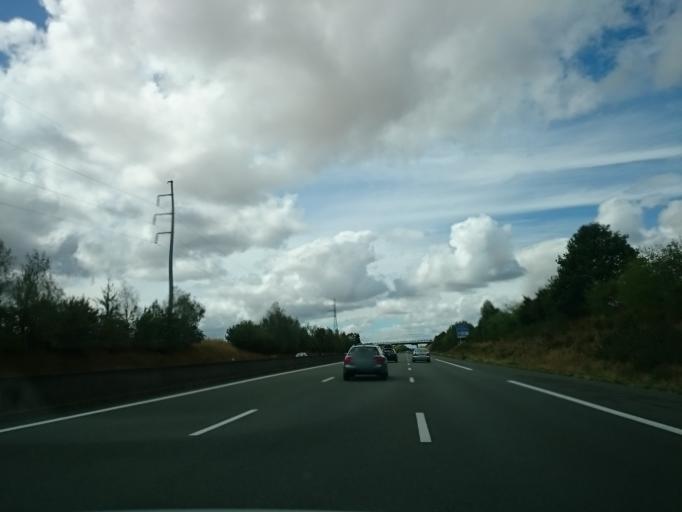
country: FR
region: Centre
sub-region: Departement d'Eure-et-Loir
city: Yevres
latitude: 48.2815
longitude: 1.2267
